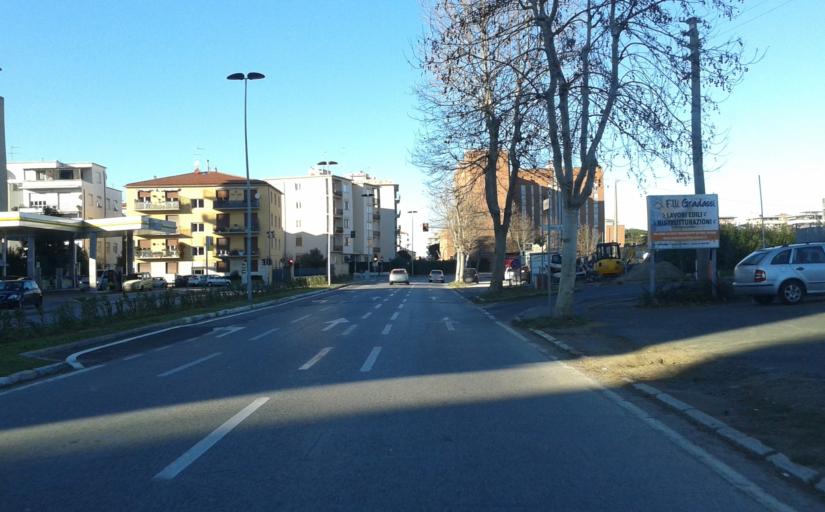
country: IT
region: Tuscany
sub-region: Provincia di Livorno
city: Livorno
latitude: 43.5364
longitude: 10.3231
